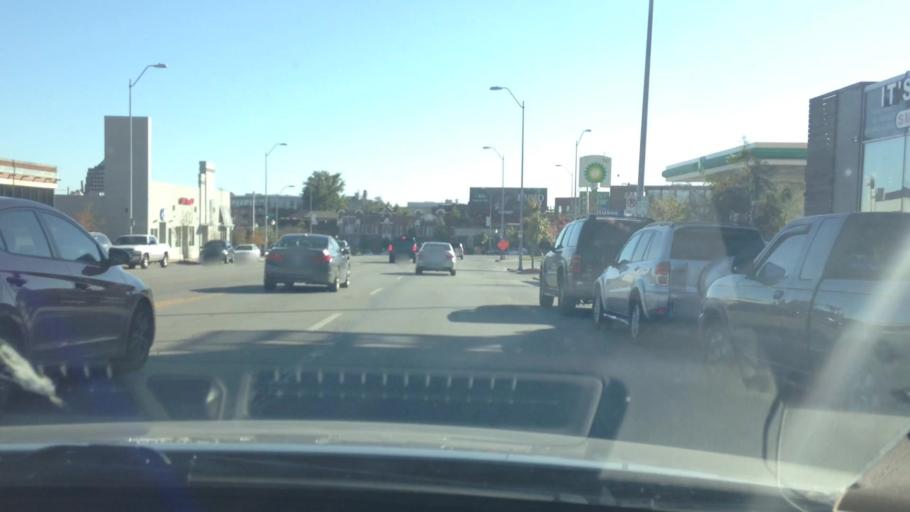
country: US
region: Kansas
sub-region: Johnson County
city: Westwood
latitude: 39.0553
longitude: -94.5910
